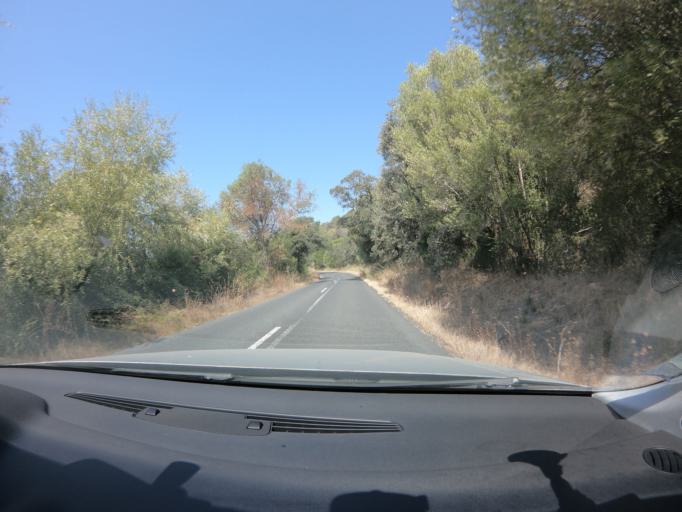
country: PT
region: Setubal
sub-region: Alcacer do Sal
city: Alcacer do Sal
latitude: 38.2764
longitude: -8.3765
